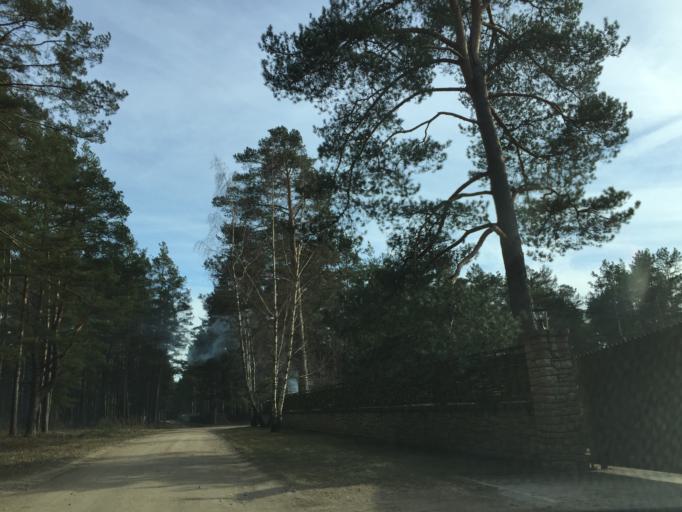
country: LV
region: Adazi
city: Adazi
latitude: 57.1237
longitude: 24.3363
